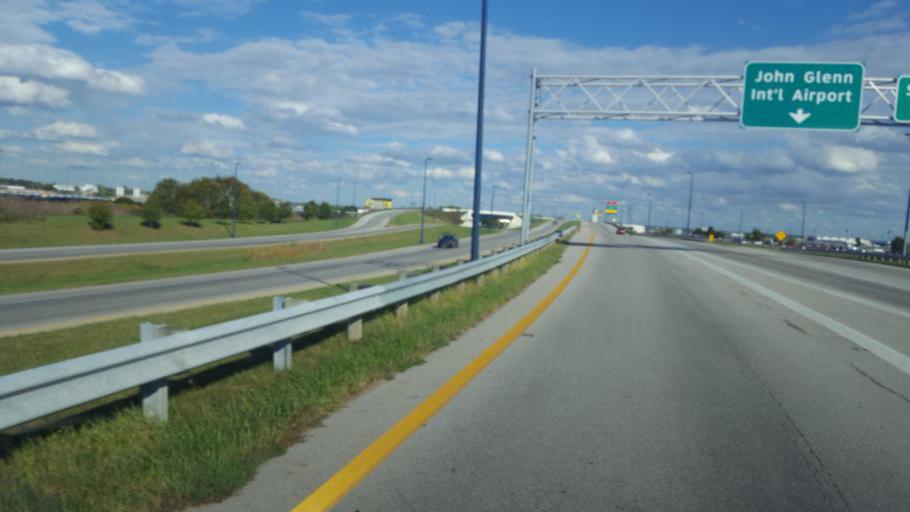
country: US
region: Ohio
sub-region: Franklin County
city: Bexley
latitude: 39.9999
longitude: -82.9189
